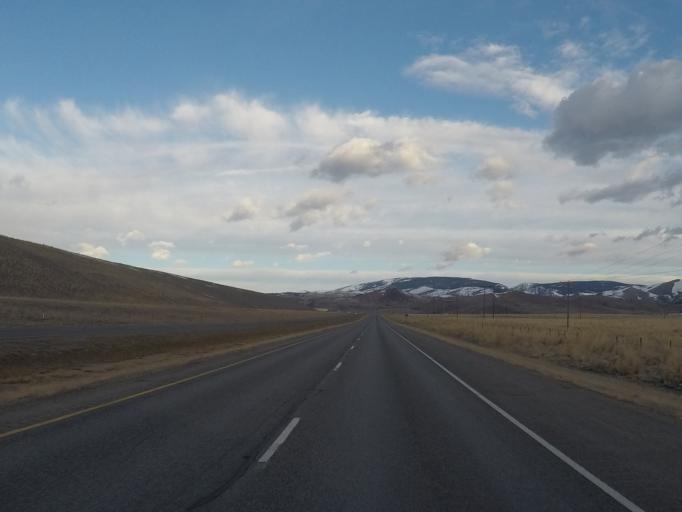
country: US
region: Montana
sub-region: Deer Lodge County
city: Anaconda
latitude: 46.1220
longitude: -112.8824
